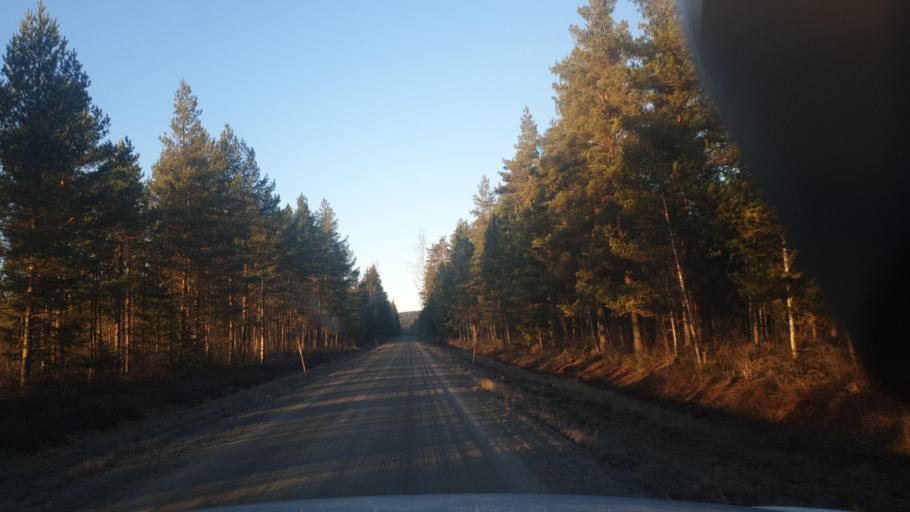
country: SE
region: Vaermland
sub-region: Eda Kommun
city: Charlottenberg
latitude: 59.9555
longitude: 12.5131
